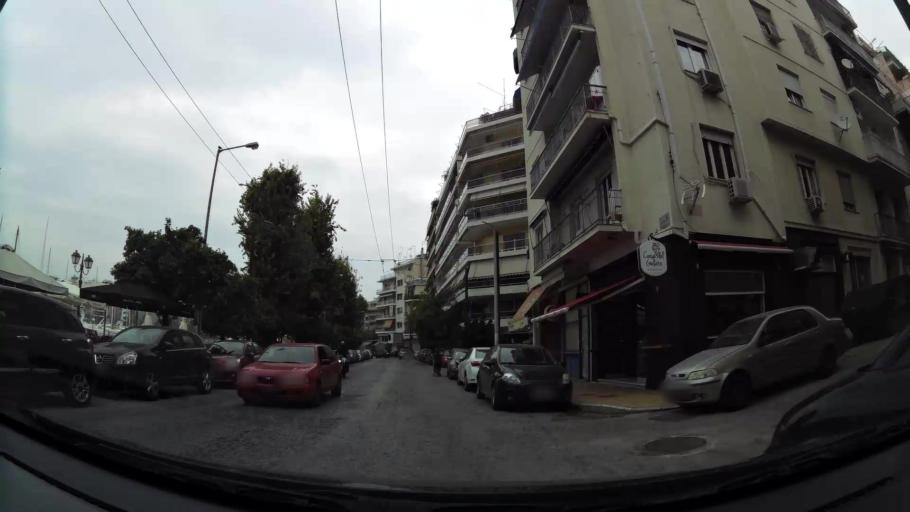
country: GR
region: Attica
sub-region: Nomos Attikis
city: Piraeus
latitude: 37.9377
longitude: 23.6508
